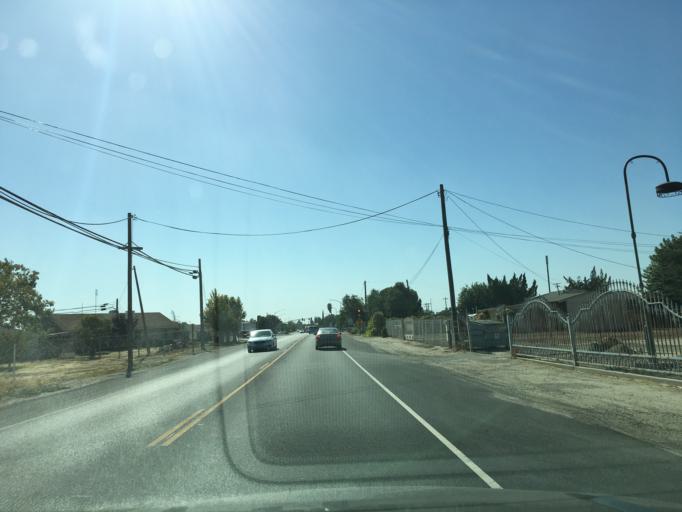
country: US
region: California
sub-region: Madera County
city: Madera
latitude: 36.9754
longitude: -120.0400
